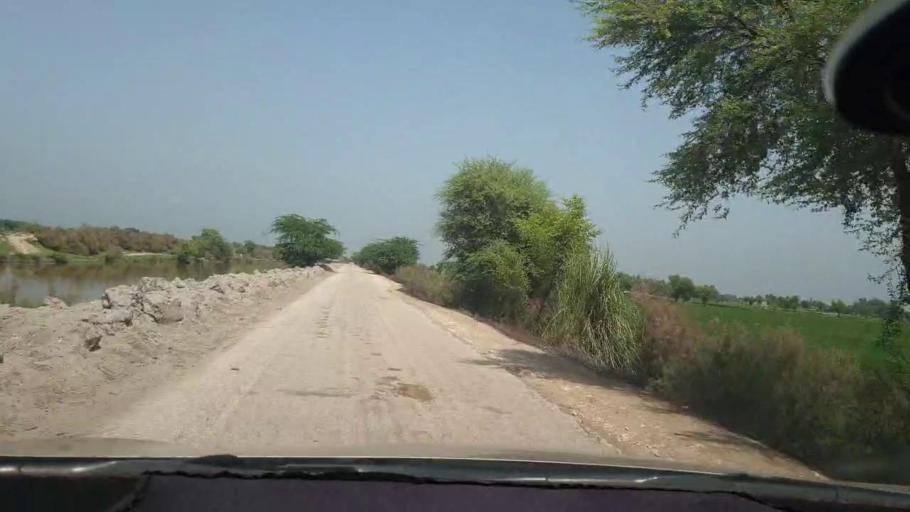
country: PK
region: Sindh
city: Kambar
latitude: 27.6662
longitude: 67.8920
